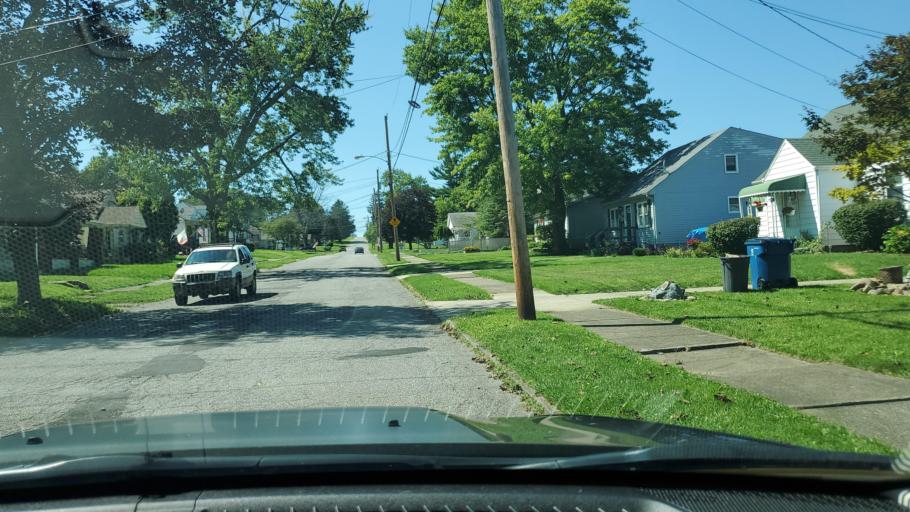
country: US
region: Ohio
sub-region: Mahoning County
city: Struthers
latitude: 41.0587
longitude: -80.6085
